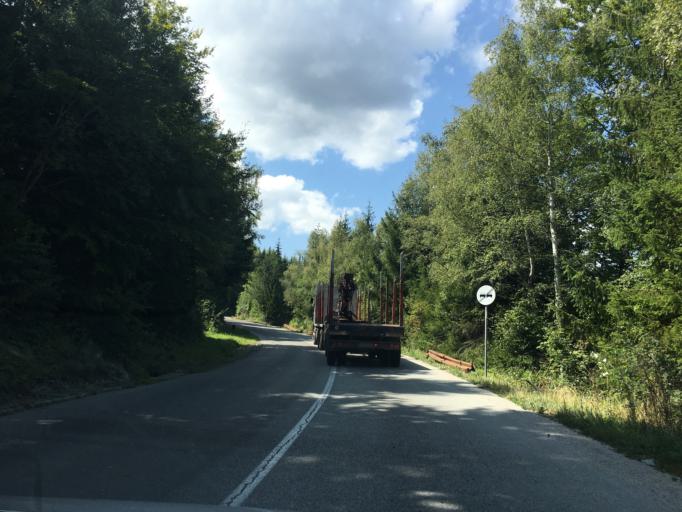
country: RS
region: Central Serbia
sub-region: Zlatiborski Okrug
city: Prijepolje
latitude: 43.3305
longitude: 19.5374
